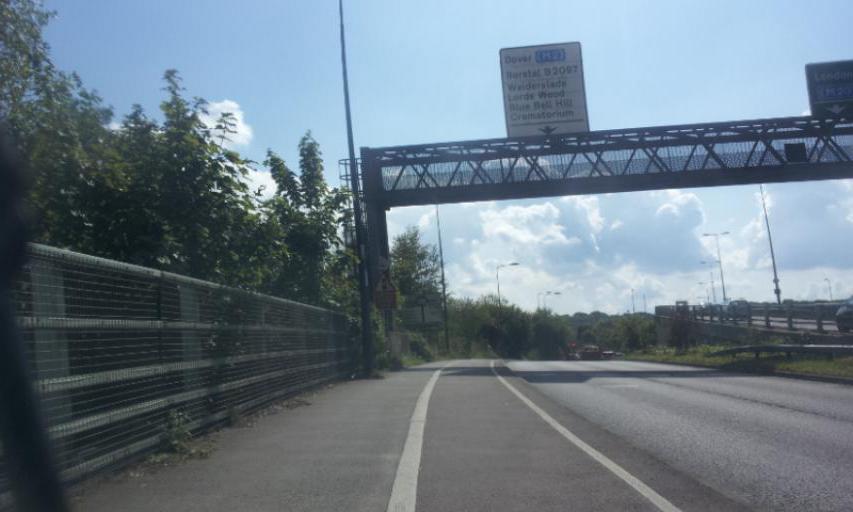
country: GB
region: England
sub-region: Kent
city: Chatham
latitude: 51.3438
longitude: 0.5076
